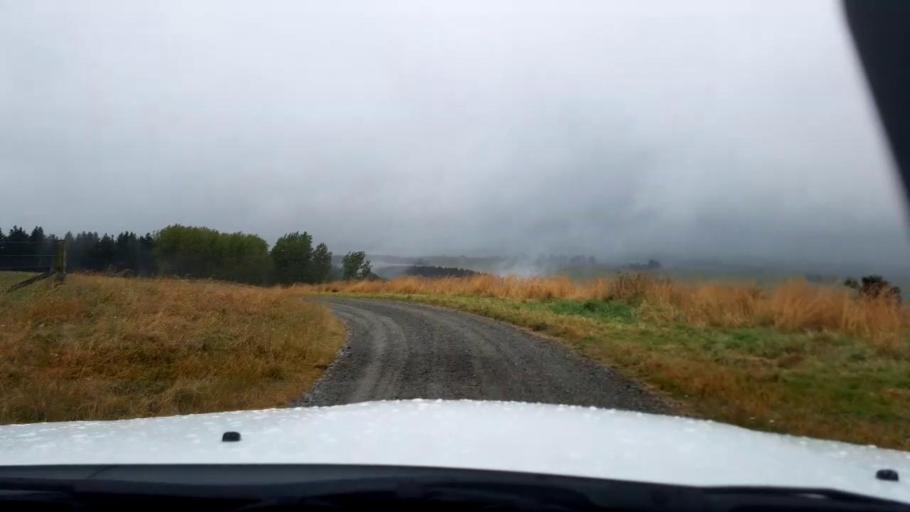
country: NZ
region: Canterbury
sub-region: Timaru District
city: Pleasant Point
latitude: -44.1762
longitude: 171.0908
